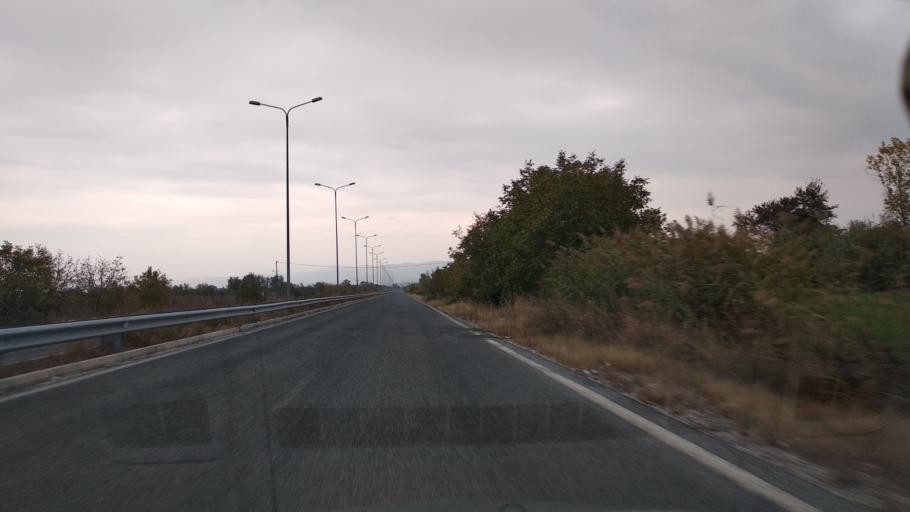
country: GR
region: Thessaly
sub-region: Trikala
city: Pyrgetos
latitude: 39.5600
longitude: 21.7351
